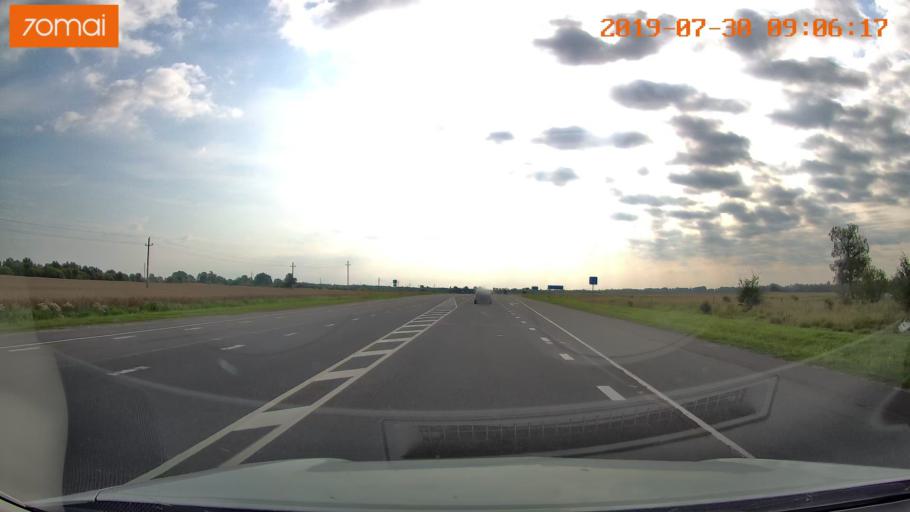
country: RU
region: Kaliningrad
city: Gusev
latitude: 54.6094
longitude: 22.3320
